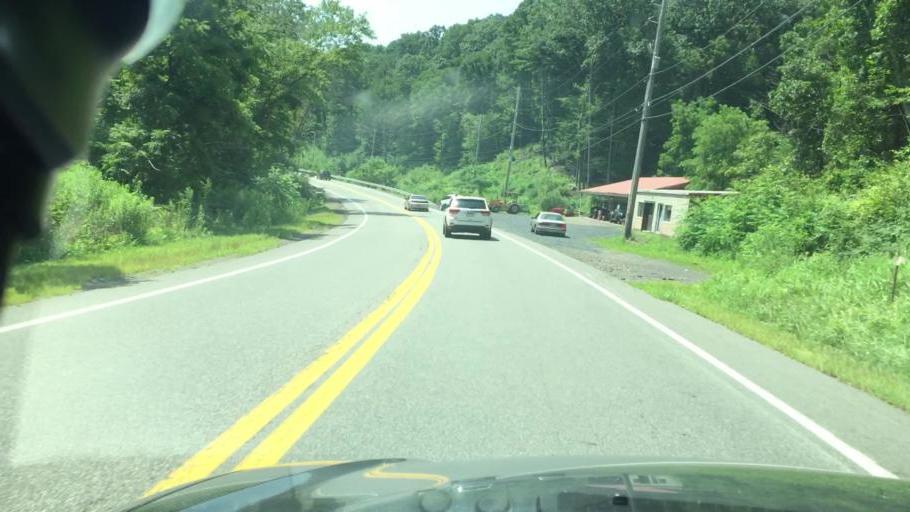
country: US
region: Pennsylvania
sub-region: Columbia County
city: Catawissa
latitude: 40.9114
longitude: -76.4758
